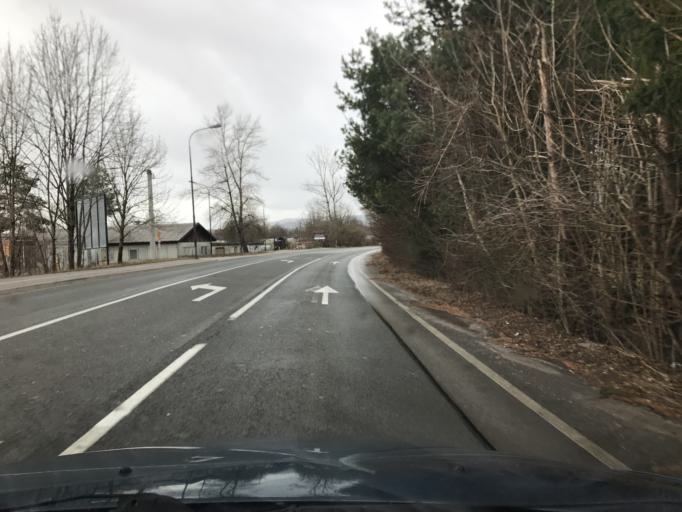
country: SI
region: Ljubljana
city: Ljubljana
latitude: 46.0992
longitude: 14.5155
